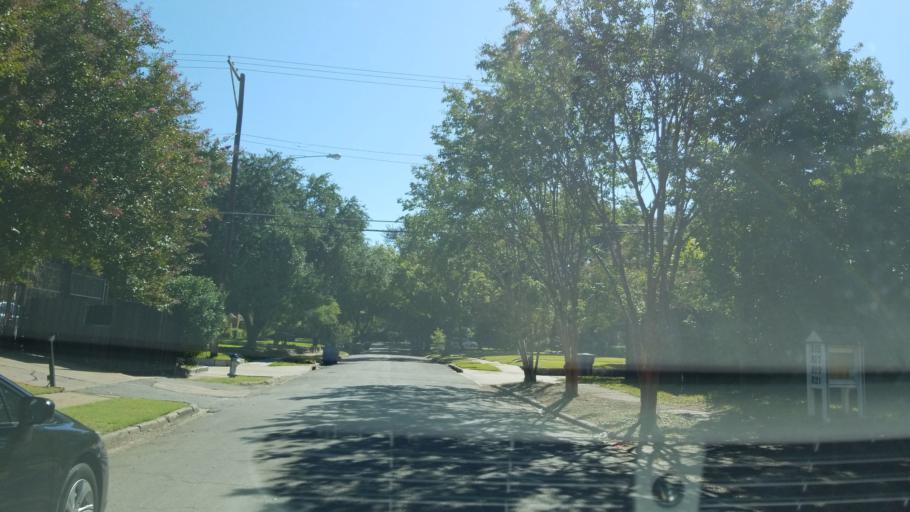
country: US
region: Texas
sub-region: Dallas County
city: Highland Park
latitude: 32.8094
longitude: -96.7577
